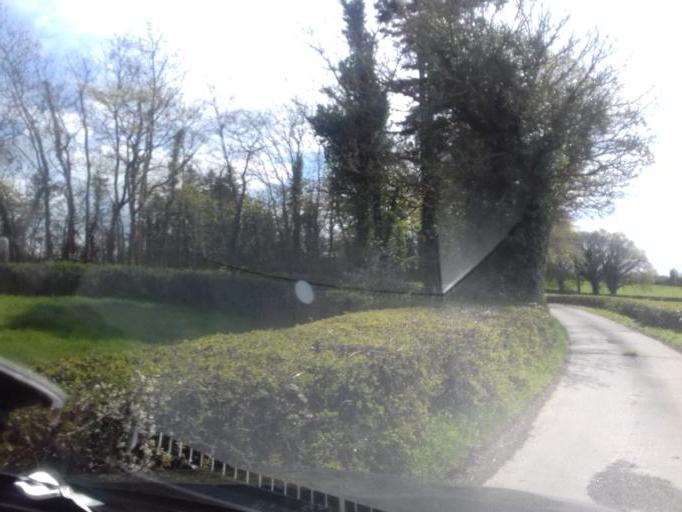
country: GB
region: Northern Ireland
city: Lisnaskea
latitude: 54.1862
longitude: -7.4886
